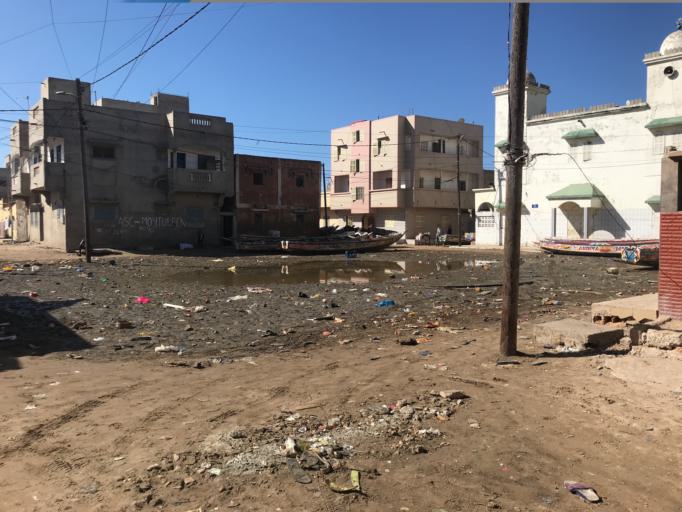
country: SN
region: Saint-Louis
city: Saint-Louis
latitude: 16.0327
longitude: -16.5081
